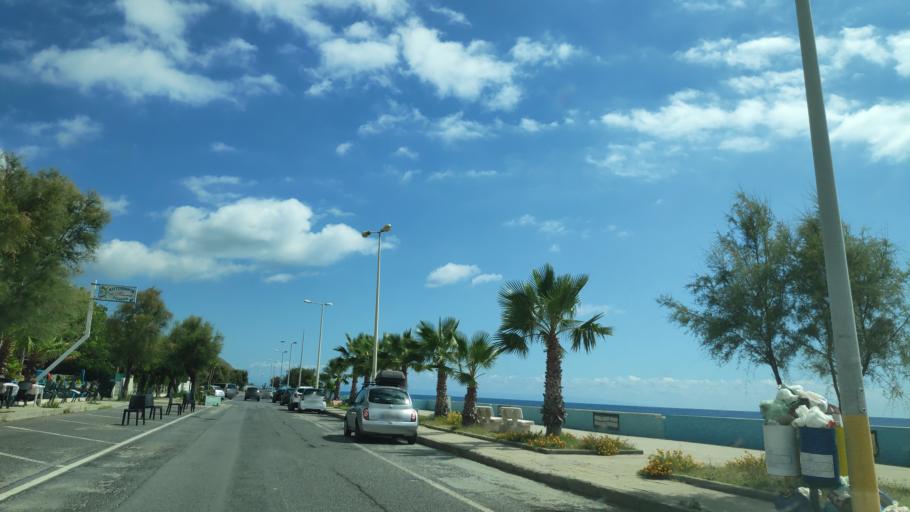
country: IT
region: Calabria
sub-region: Provincia di Cosenza
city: Amantea
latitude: 39.1274
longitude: 16.0702
